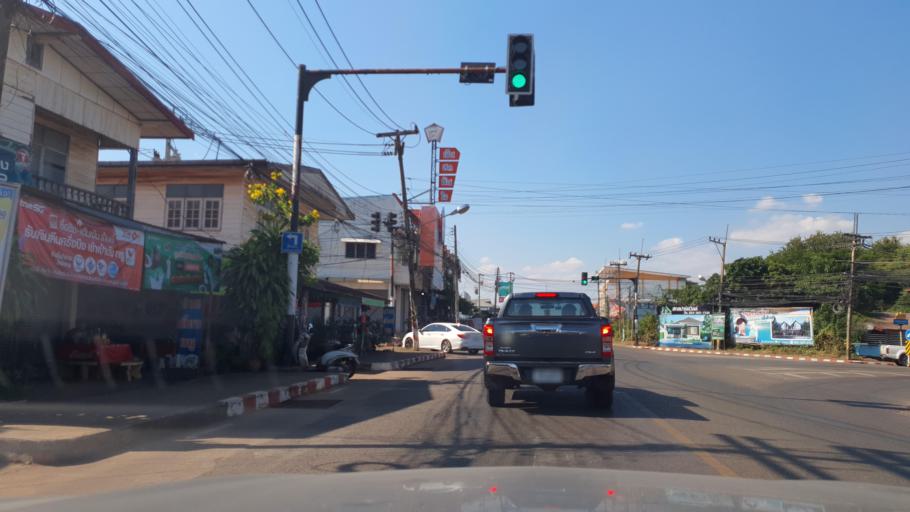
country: TH
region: Sakon Nakhon
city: Sakon Nakhon
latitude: 17.1638
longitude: 104.1237
